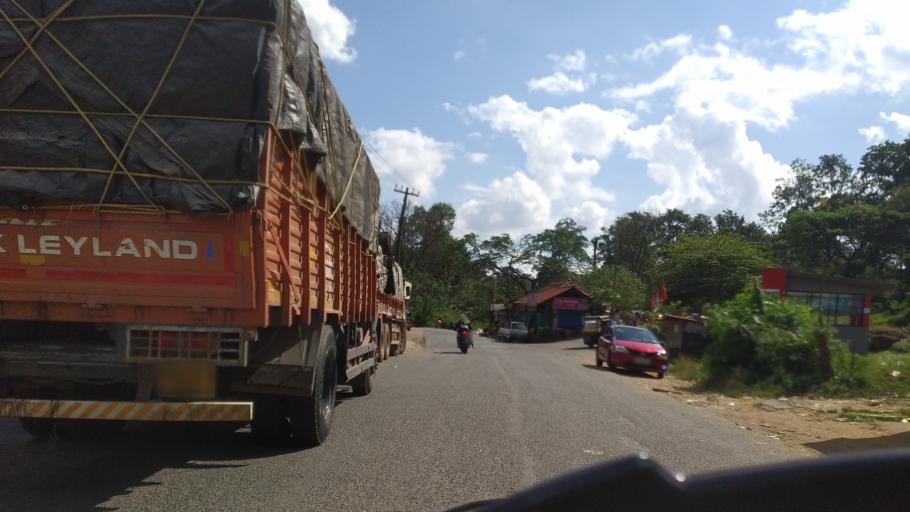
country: IN
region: Karnataka
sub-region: Kodagu
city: Ponnampet
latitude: 11.9575
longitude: 76.0628
